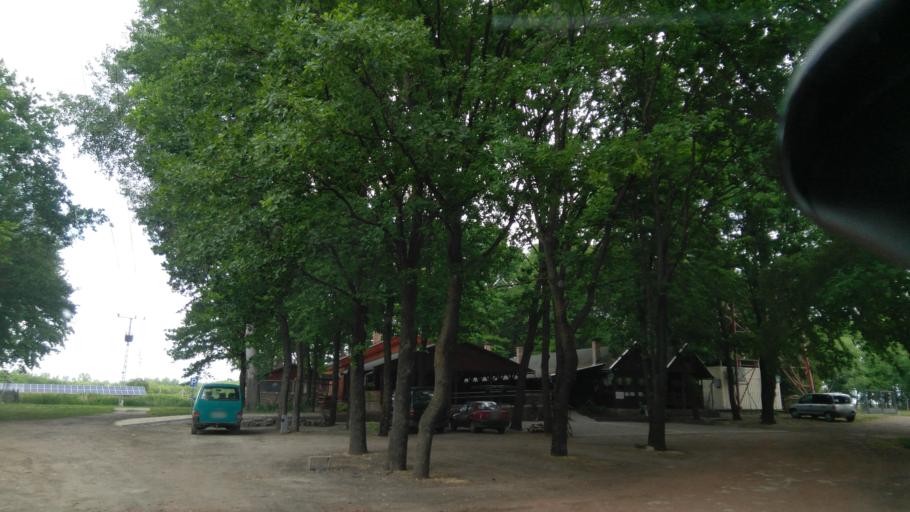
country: HU
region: Bekes
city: Mezohegyes
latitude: 46.3108
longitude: 20.8271
